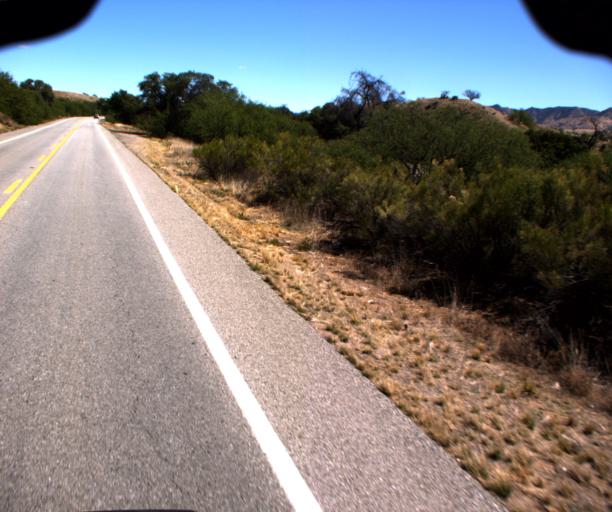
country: US
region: Arizona
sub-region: Santa Cruz County
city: Rio Rico
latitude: 31.4555
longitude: -110.8311
